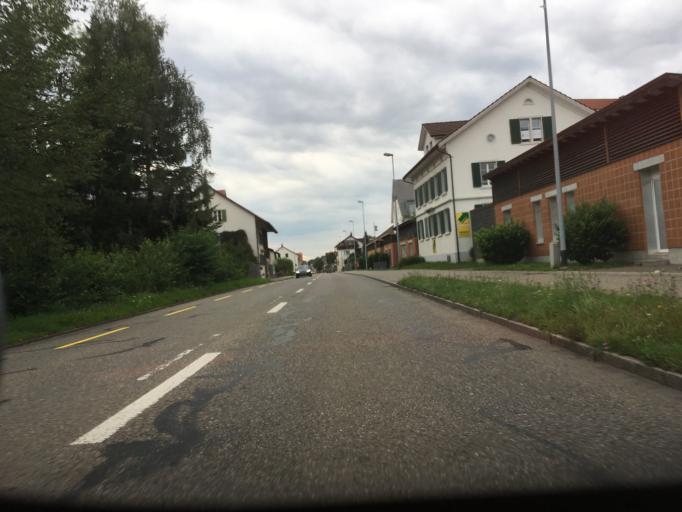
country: CH
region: Zurich
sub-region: Bezirk Pfaeffikon
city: Fehraltorf
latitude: 47.3848
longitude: 8.7570
